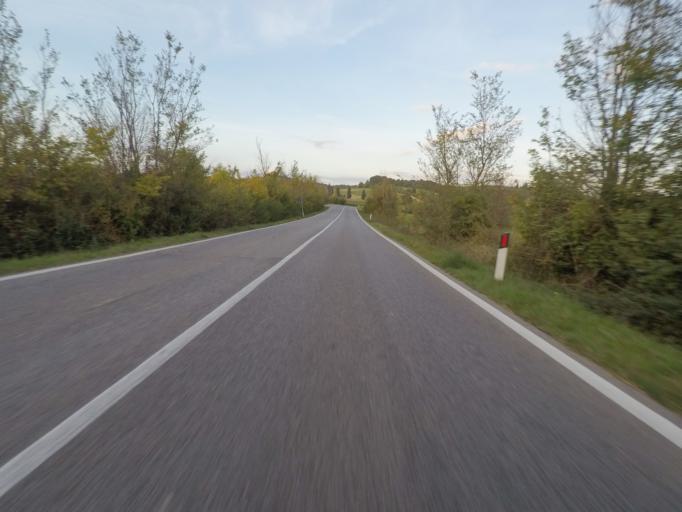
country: IT
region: Tuscany
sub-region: Provincia di Siena
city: Pienza
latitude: 43.0956
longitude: 11.6899
